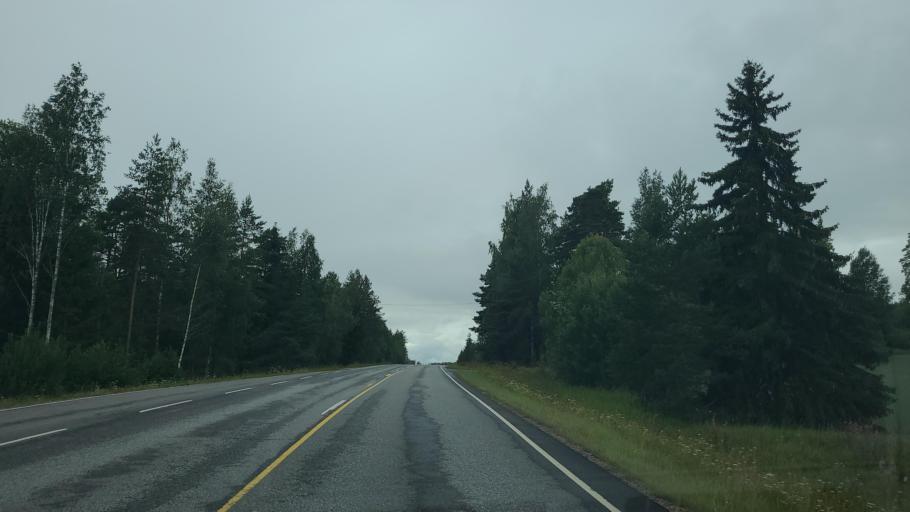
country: FI
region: Varsinais-Suomi
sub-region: Aboland-Turunmaa
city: Kimito
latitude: 60.1912
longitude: 22.6900
